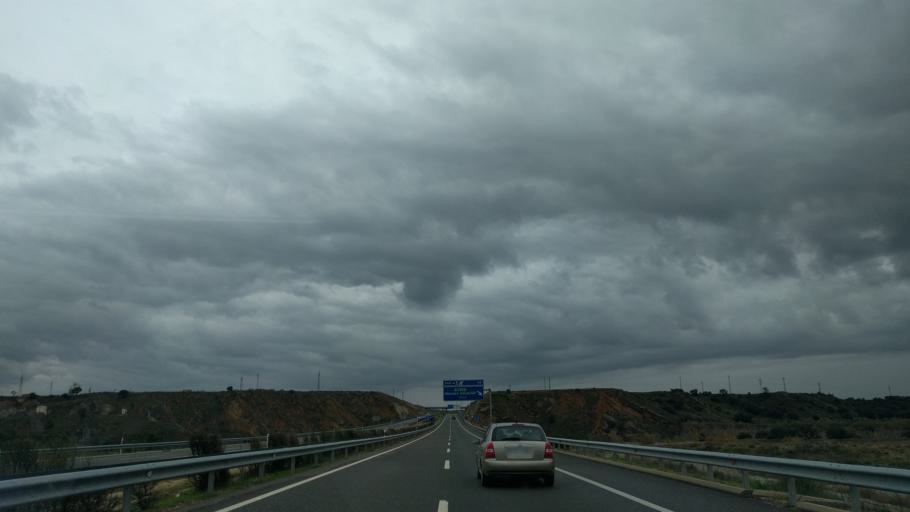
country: ES
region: Aragon
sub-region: Provincia de Huesca
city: Castejon del Puente
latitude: 41.9572
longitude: 0.1771
